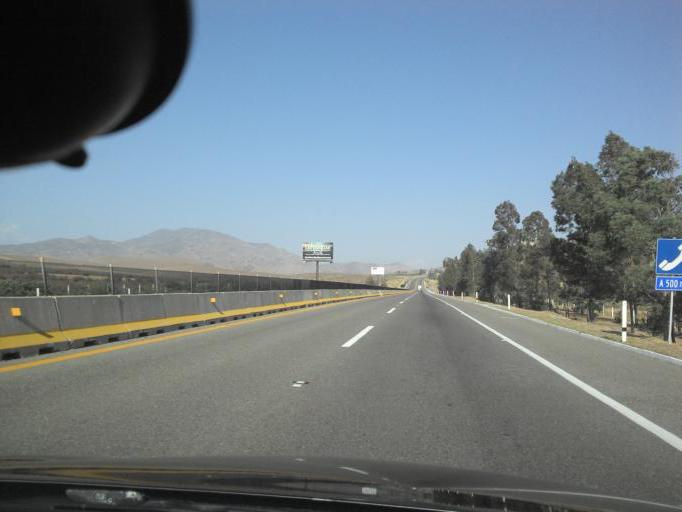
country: MX
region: Baja California
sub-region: Tijuana
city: El Nino
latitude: 32.5457
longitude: -116.7874
